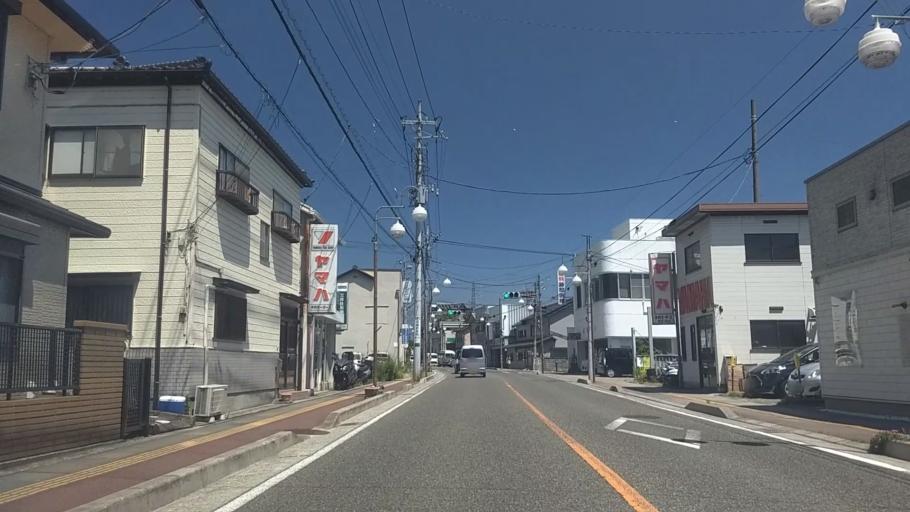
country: JP
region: Yamanashi
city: Nirasaki
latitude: 35.7119
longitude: 138.4493
